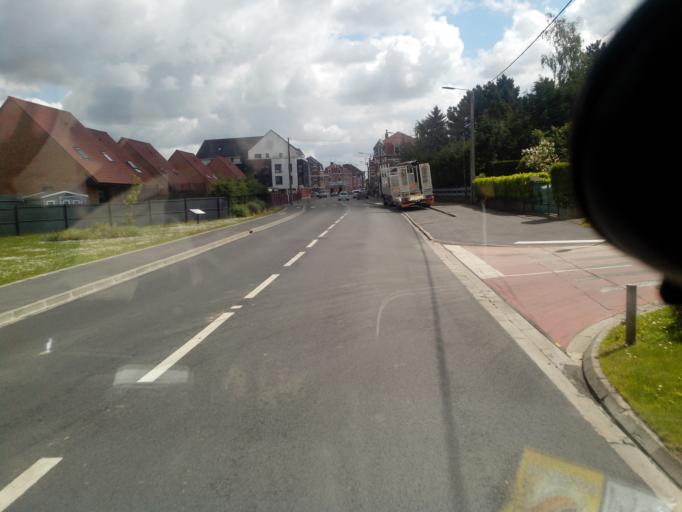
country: FR
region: Nord-Pas-de-Calais
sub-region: Departement du Nord
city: Erquinghem-Lys
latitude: 50.6755
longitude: 2.8356
